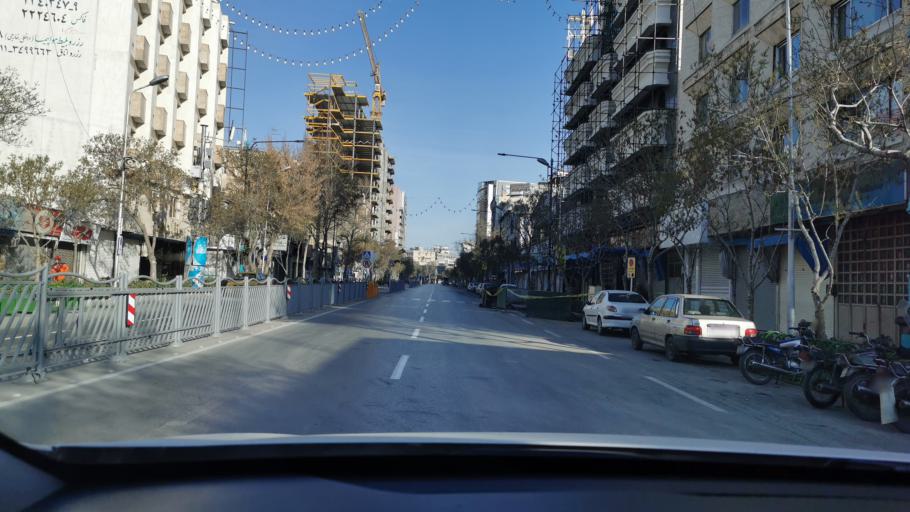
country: IR
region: Razavi Khorasan
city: Mashhad
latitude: 36.2877
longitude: 59.6090
